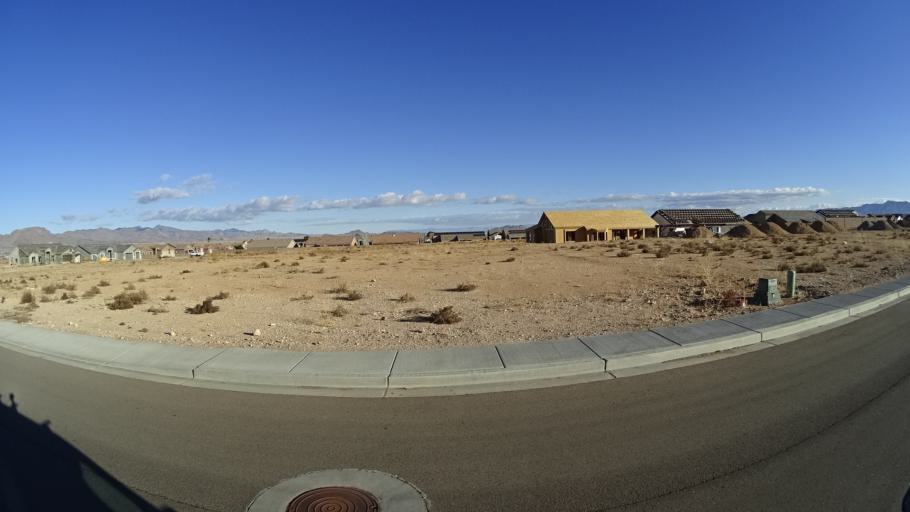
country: US
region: Arizona
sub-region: Mohave County
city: New Kingman-Butler
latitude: 35.2176
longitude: -113.9735
